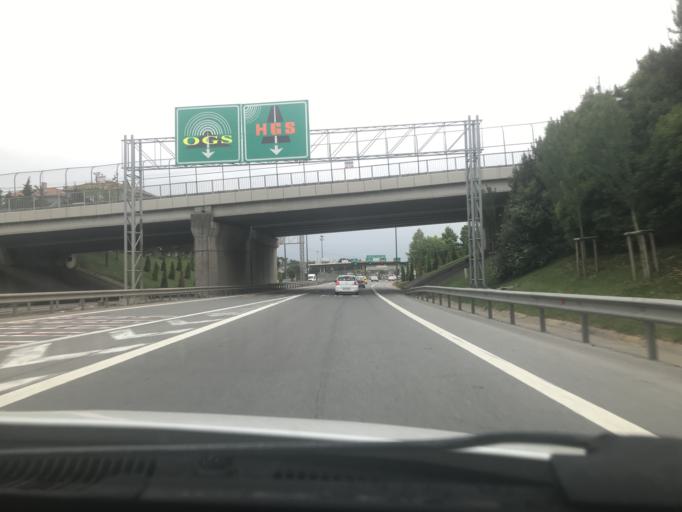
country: TR
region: Istanbul
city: Sultanbeyli
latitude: 40.9346
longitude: 29.3311
